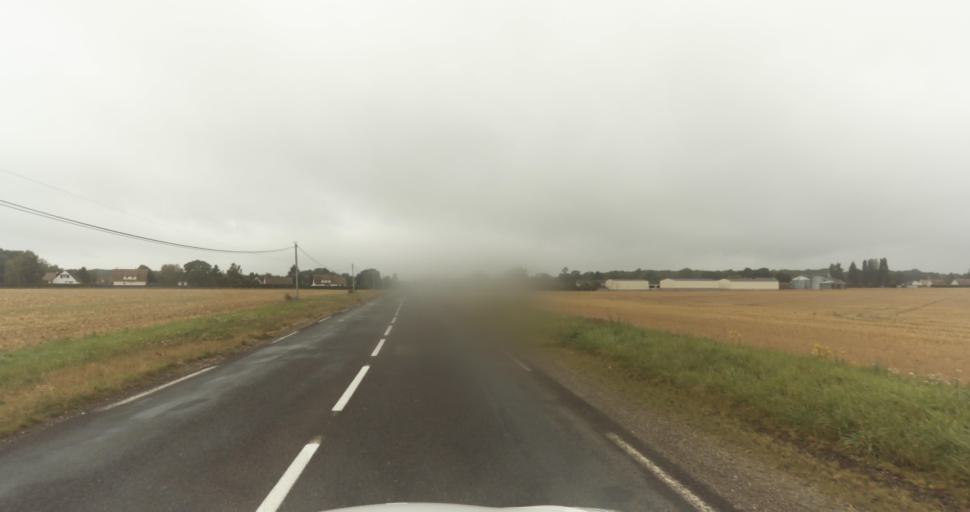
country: FR
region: Haute-Normandie
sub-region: Departement de l'Eure
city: Normanville
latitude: 49.0850
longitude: 1.1861
